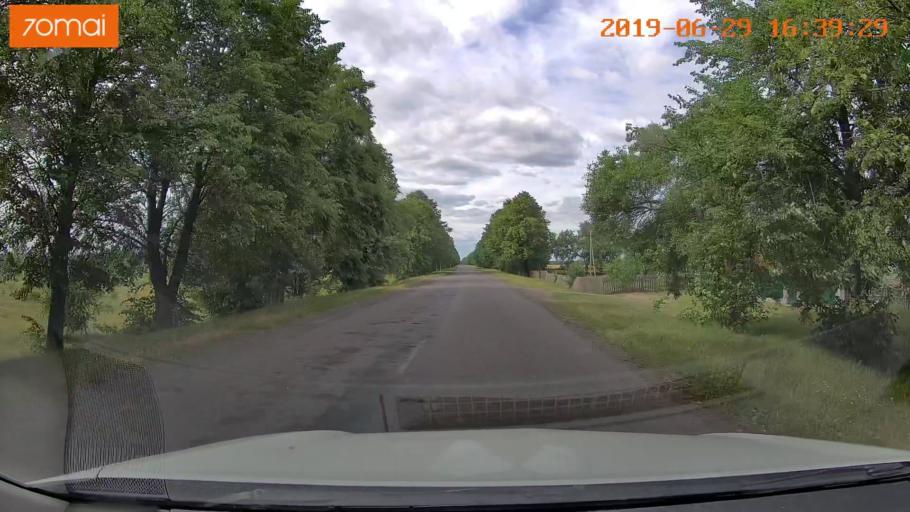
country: BY
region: Brest
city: Luninyets
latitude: 52.2430
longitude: 27.0162
